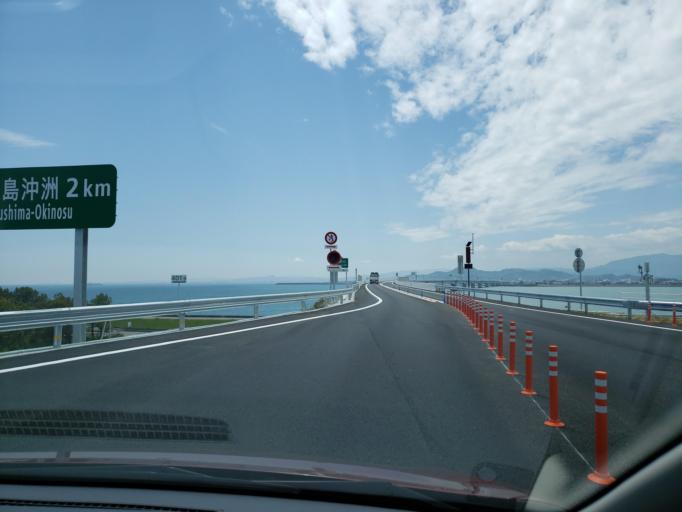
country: JP
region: Tokushima
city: Tokushima-shi
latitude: 34.0854
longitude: 134.6019
